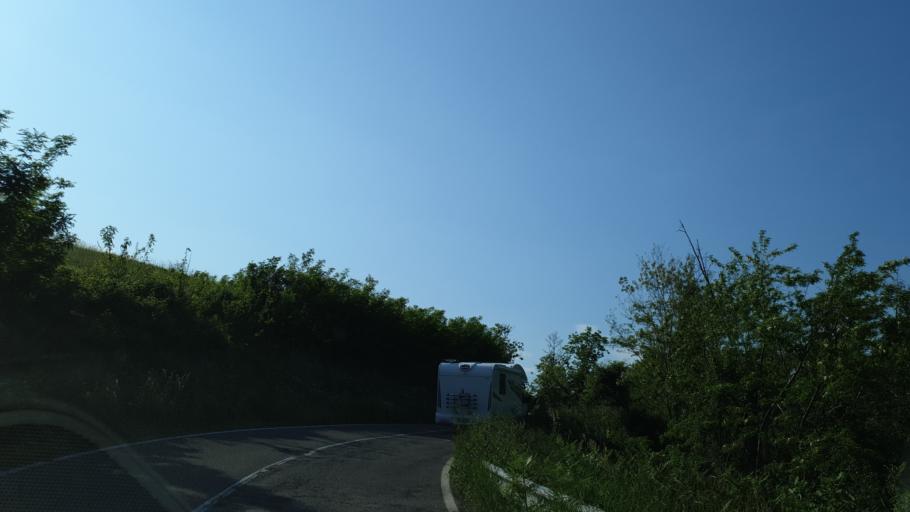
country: IT
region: Tuscany
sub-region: Province of Arezzo
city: Stia
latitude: 43.7751
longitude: 11.6973
